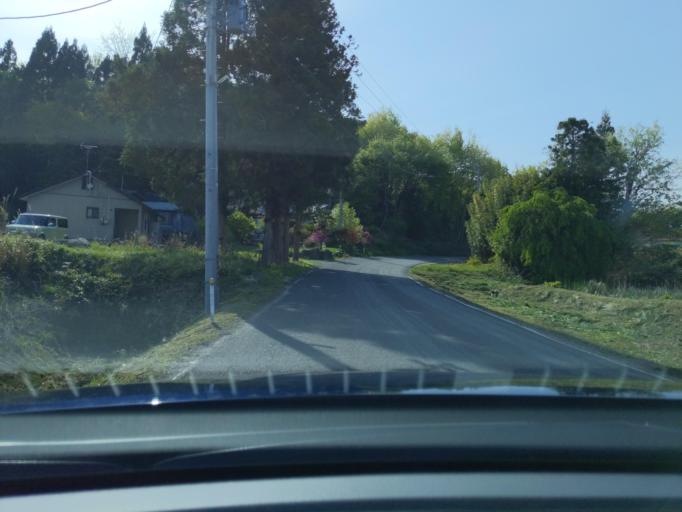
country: JP
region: Fukushima
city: Sukagawa
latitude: 37.2968
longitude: 140.4151
